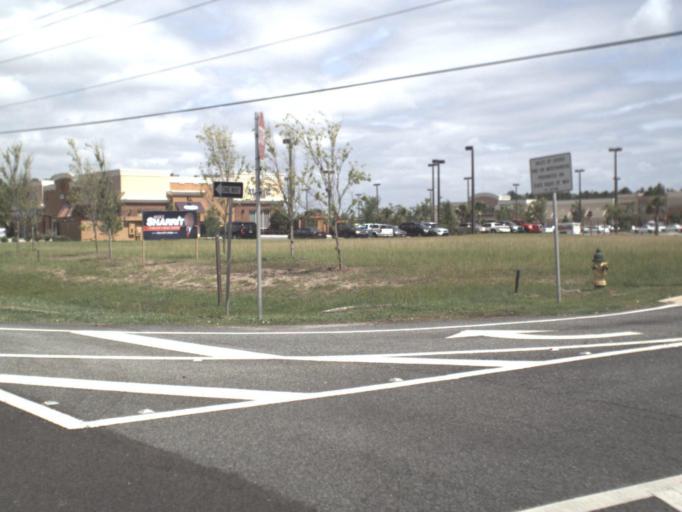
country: US
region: Florida
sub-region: Nassau County
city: Yulee
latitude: 30.6254
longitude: -81.5442
